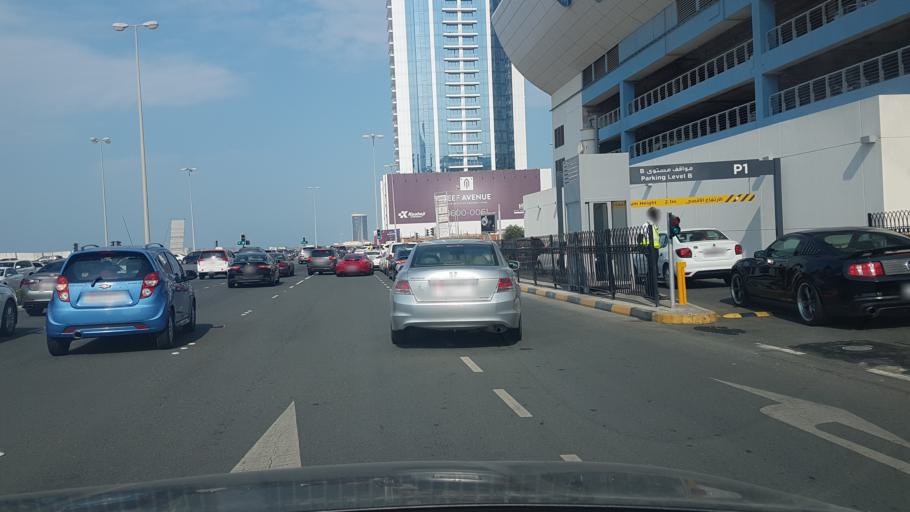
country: BH
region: Manama
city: Jidd Hafs
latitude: 26.2341
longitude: 50.5515
